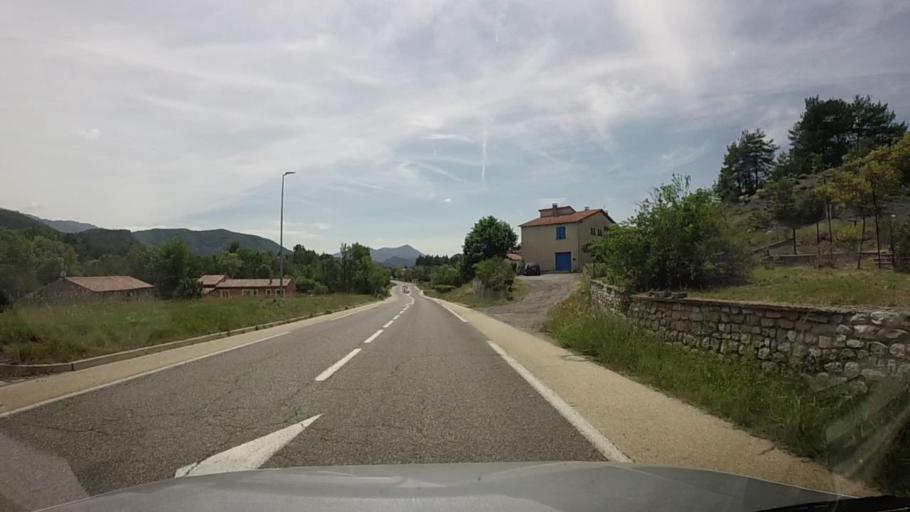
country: FR
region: Provence-Alpes-Cote d'Azur
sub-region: Departement des Alpes-de-Haute-Provence
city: Le Brusquet
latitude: 44.1543
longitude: 6.2976
